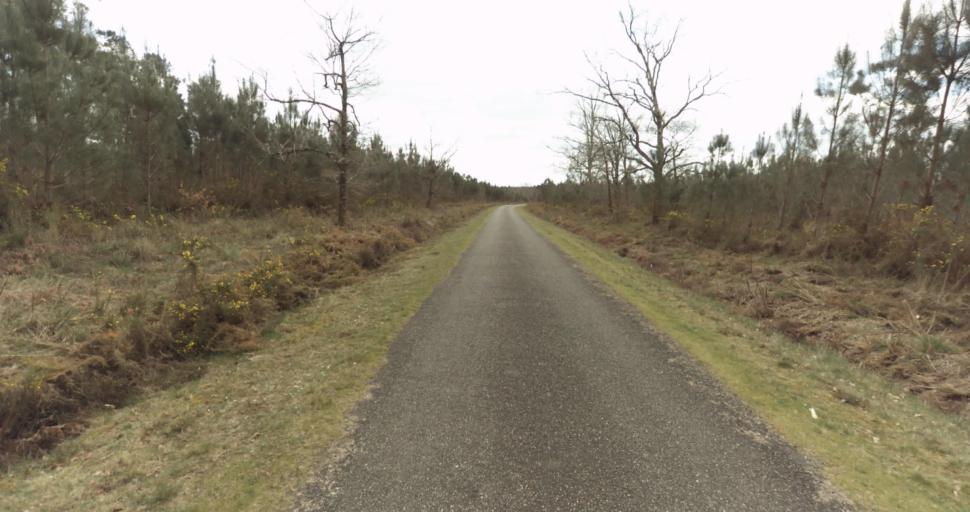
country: FR
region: Aquitaine
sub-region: Departement des Landes
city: Roquefort
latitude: 44.0802
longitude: -0.4406
